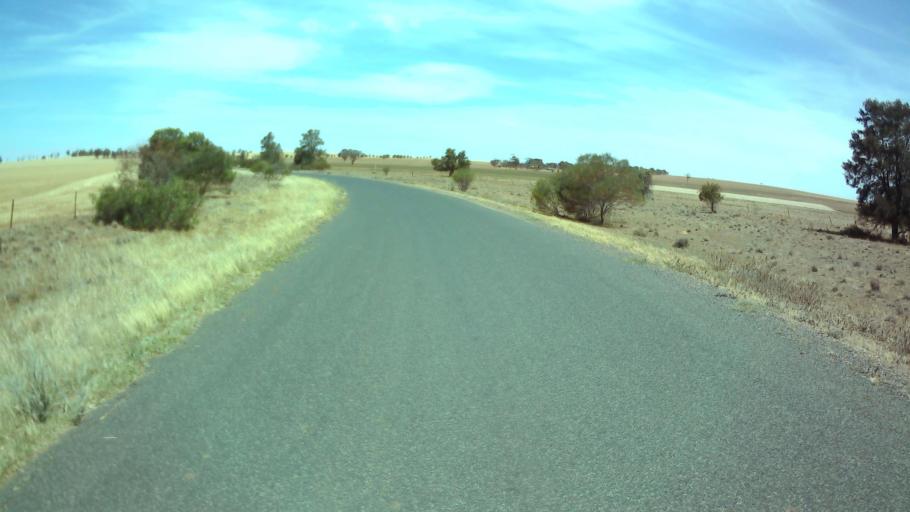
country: AU
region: New South Wales
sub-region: Weddin
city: Grenfell
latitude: -33.8895
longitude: 147.7421
